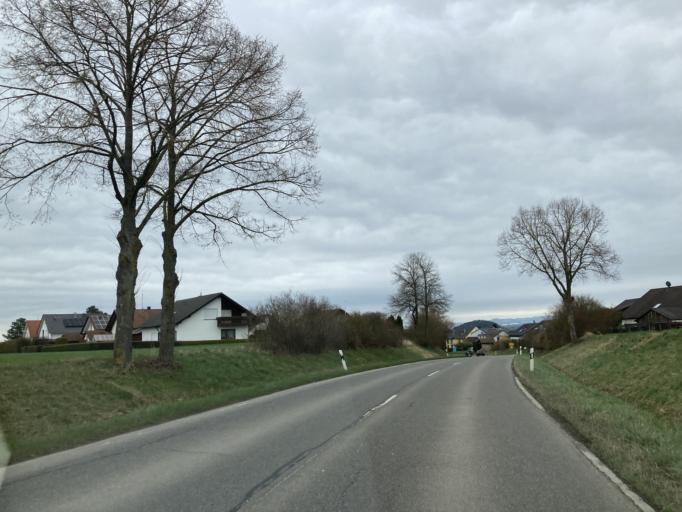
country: DE
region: Baden-Wuerttemberg
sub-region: Regierungsbezirk Stuttgart
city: Bondorf
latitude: 48.5084
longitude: 8.8689
